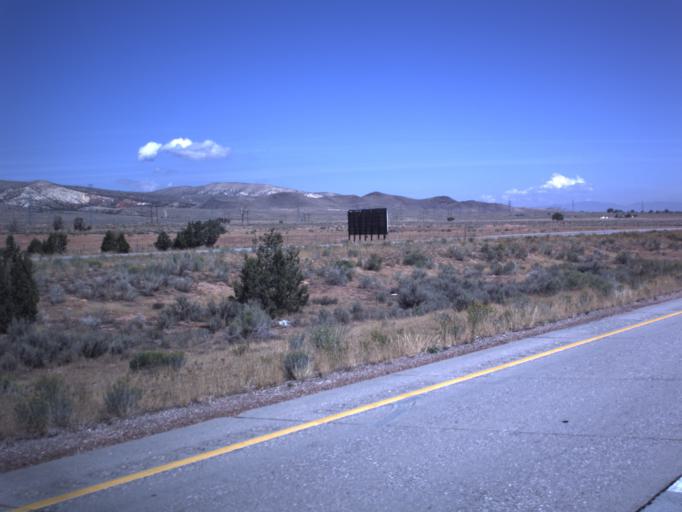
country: US
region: Utah
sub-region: Sevier County
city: Aurora
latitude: 38.8681
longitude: -111.9750
